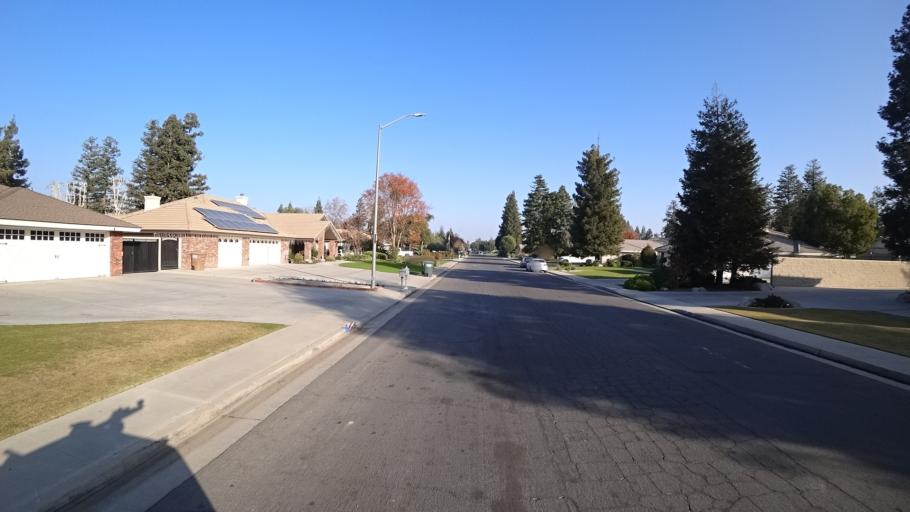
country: US
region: California
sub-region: Kern County
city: Rosedale
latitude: 35.3582
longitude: -119.1535
